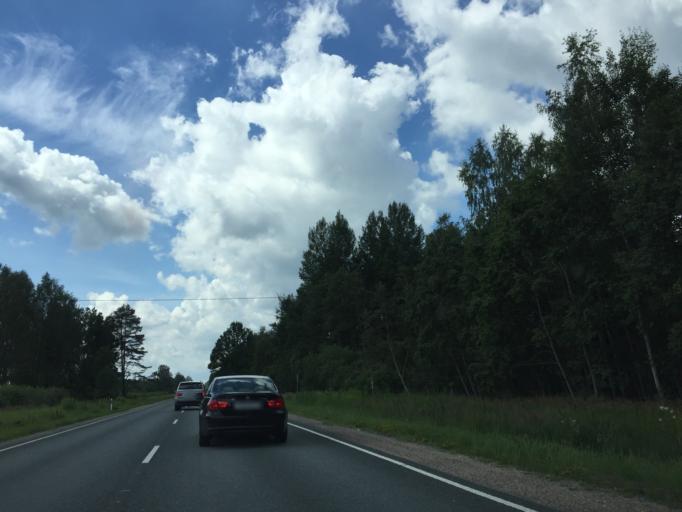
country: LV
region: Ozolnieku
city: Ozolnieki
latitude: 56.7214
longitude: 23.8451
